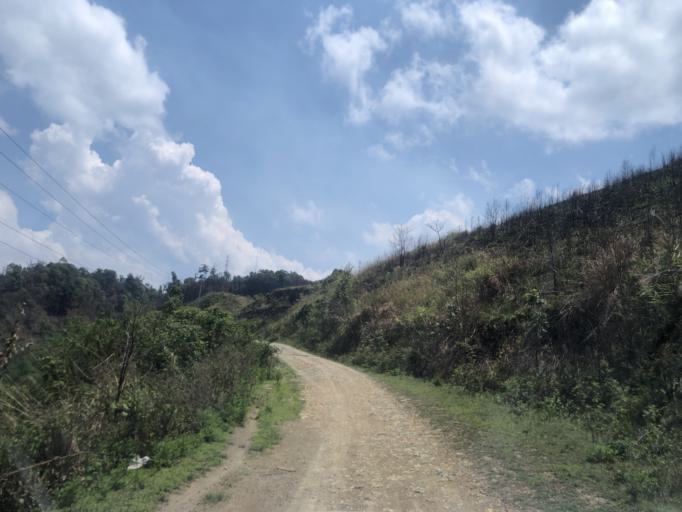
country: LA
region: Phongsali
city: Phongsali
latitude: 21.4018
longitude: 102.1889
